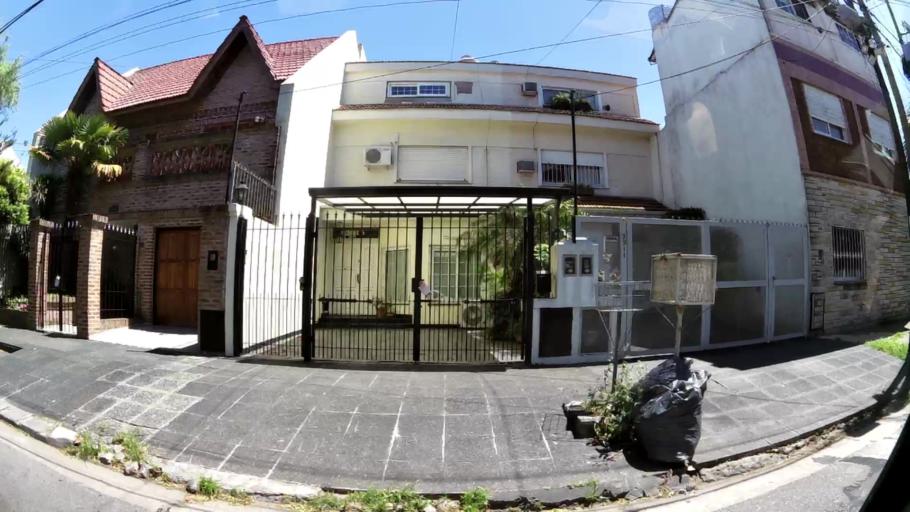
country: AR
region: Buenos Aires
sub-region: Partido de Vicente Lopez
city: Olivos
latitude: -34.5075
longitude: -58.5100
